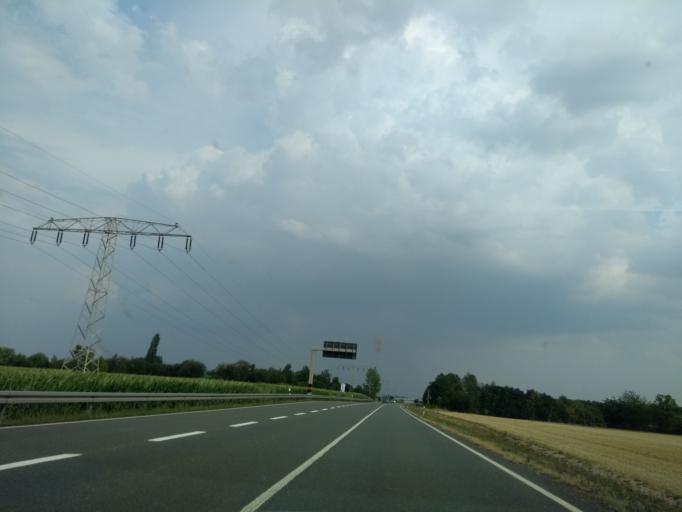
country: DE
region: Thuringia
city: Schwaara
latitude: 50.9371
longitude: 12.1180
